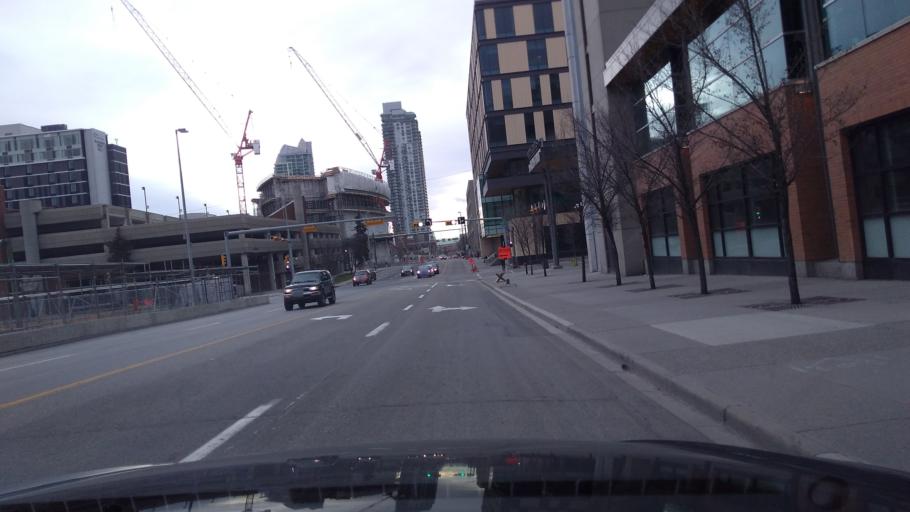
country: CA
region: Alberta
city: Calgary
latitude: 51.0479
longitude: -114.0556
